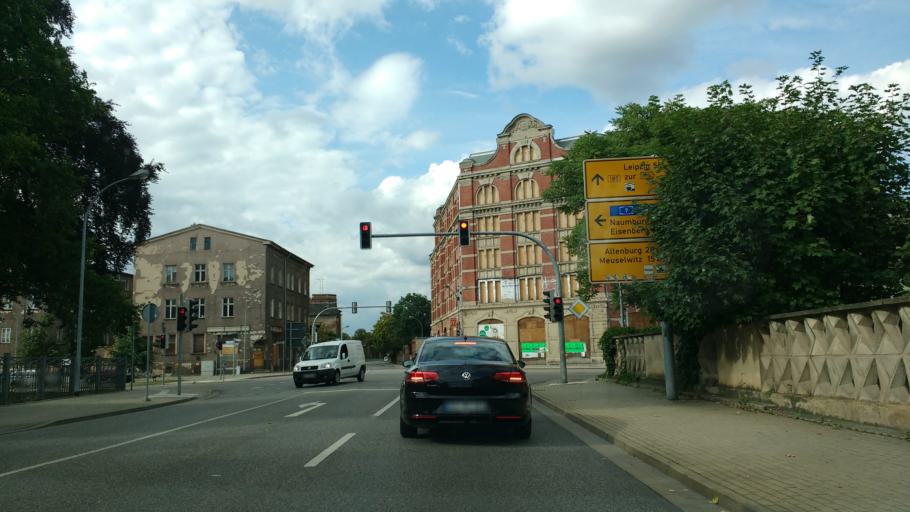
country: DE
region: Saxony-Anhalt
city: Zeitz
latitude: 51.0525
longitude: 12.1286
